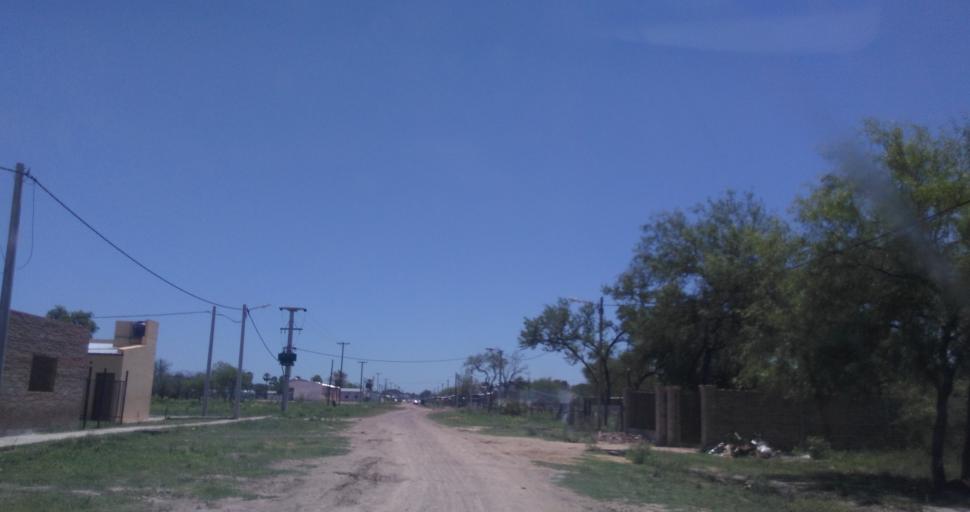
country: AR
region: Chaco
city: Fontana
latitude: -27.4794
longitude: -59.0493
